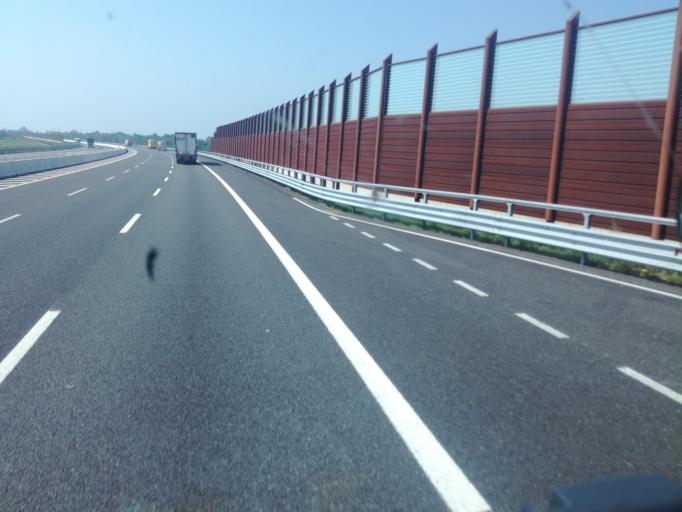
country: IT
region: Lombardy
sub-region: Provincia di Lodi
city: Cassino d'Alberi
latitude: 45.3891
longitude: 9.3764
